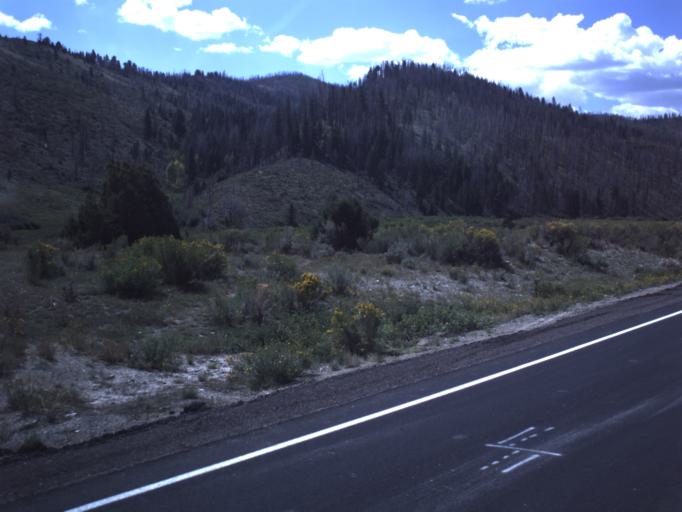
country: US
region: Utah
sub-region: Carbon County
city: Helper
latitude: 39.9270
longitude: -110.6805
